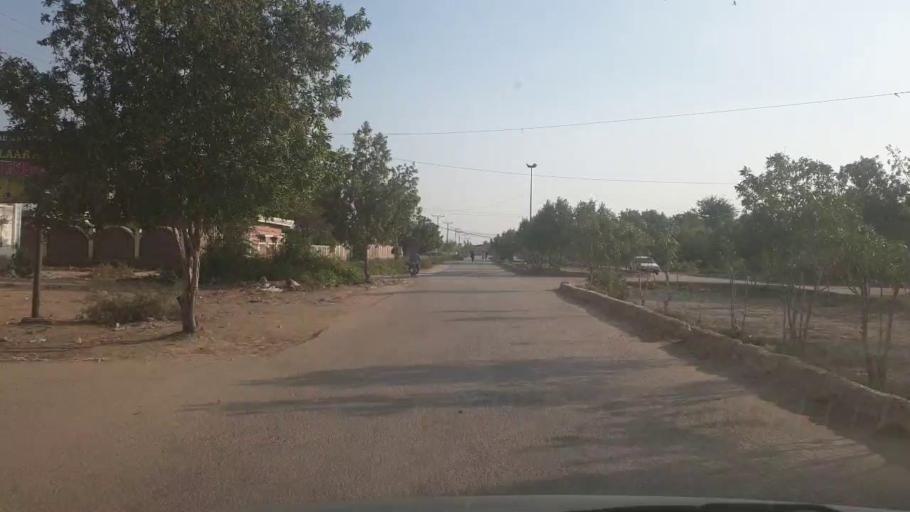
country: PK
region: Sindh
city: Badin
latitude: 24.6545
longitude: 68.8274
